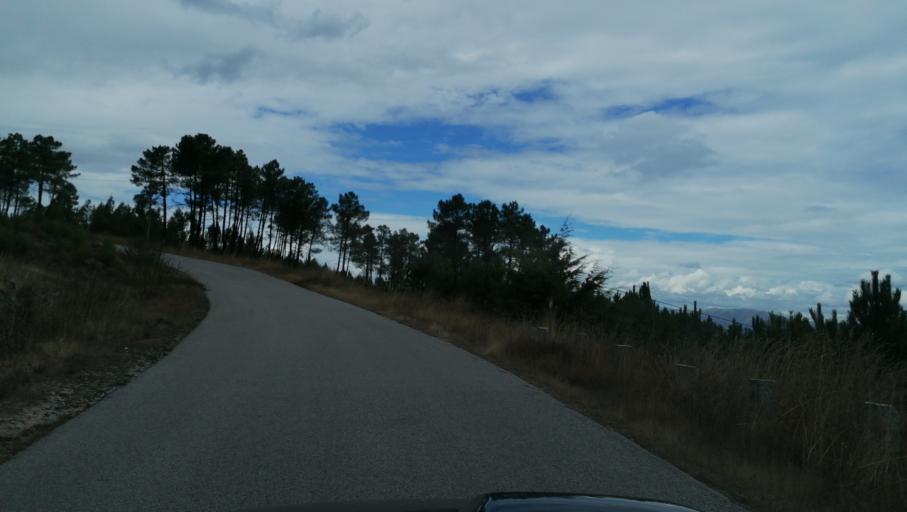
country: PT
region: Vila Real
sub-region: Vila Pouca de Aguiar
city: Vila Pouca de Aguiar
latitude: 41.5561
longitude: -7.6295
